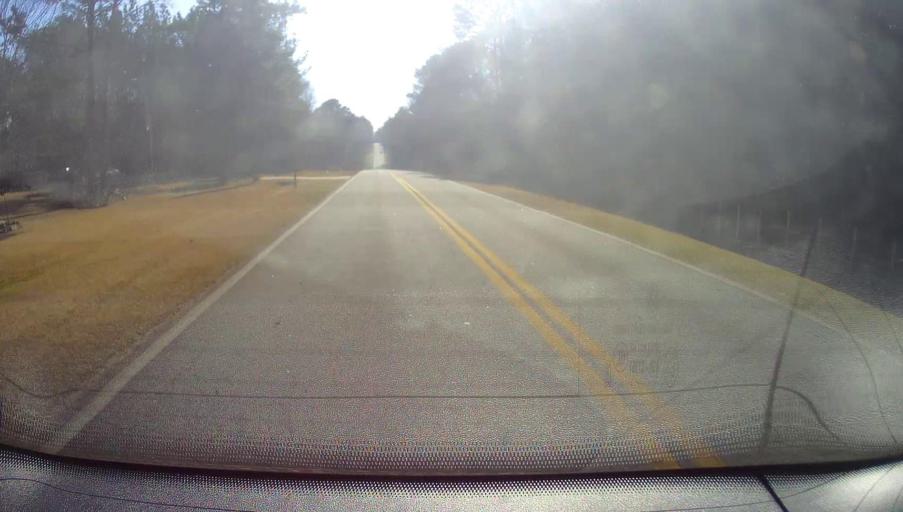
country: US
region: Georgia
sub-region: Monroe County
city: Forsyth
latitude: 33.0739
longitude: -83.8602
